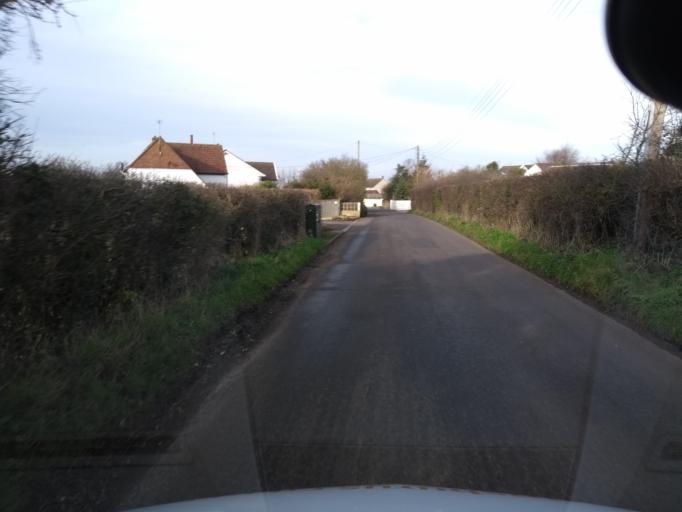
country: GB
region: England
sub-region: North Somerset
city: Bleadon
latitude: 51.3160
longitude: -2.9580
